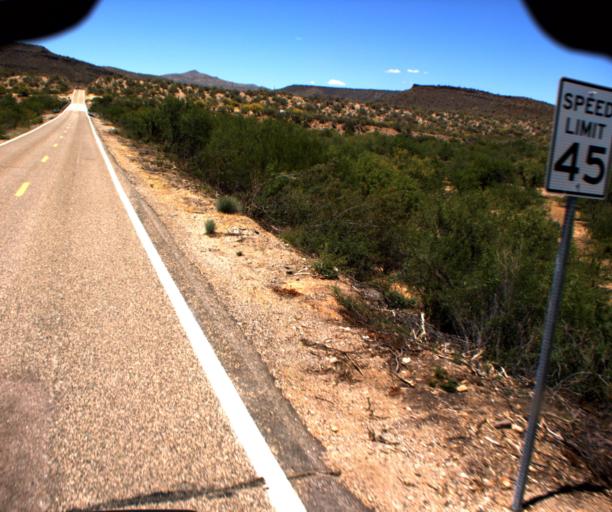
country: US
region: Arizona
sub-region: Yavapai County
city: Bagdad
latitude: 34.4790
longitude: -113.0589
